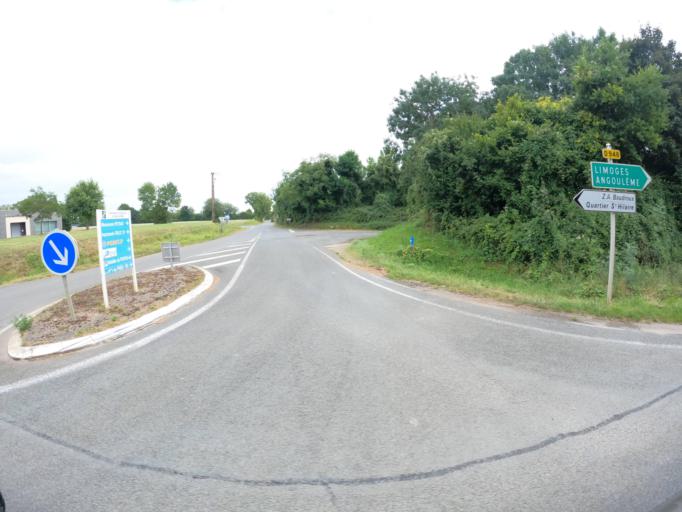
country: FR
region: Poitou-Charentes
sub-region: Departement des Deux-Sevres
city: Melle
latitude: 46.2202
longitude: -0.1560
